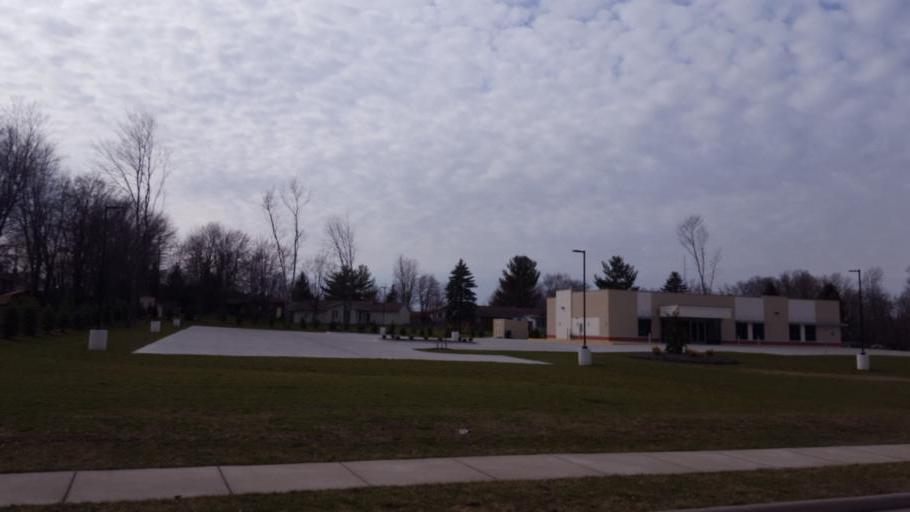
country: US
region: Ohio
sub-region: Richland County
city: Mansfield
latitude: 40.7112
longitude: -82.5369
